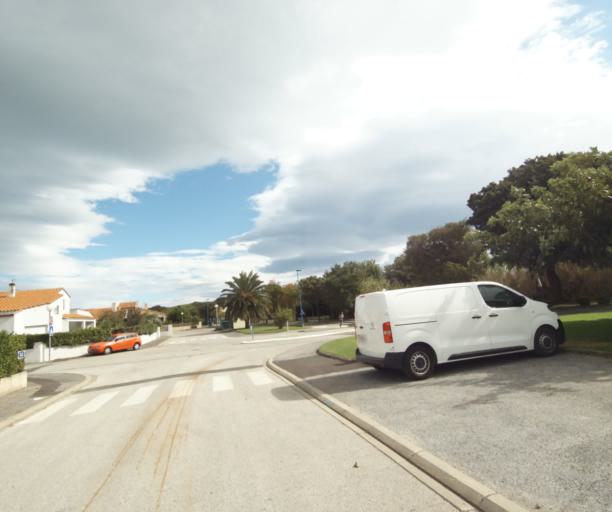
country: FR
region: Languedoc-Roussillon
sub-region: Departement des Pyrenees-Orientales
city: Argelers
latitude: 42.5518
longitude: 3.0246
